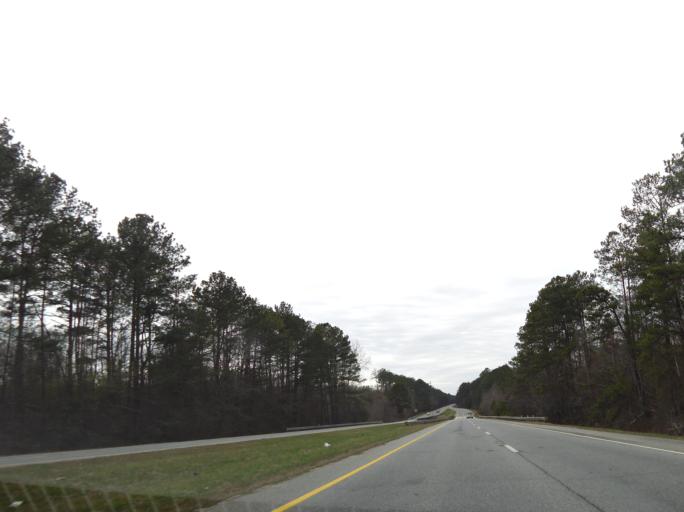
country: US
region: Georgia
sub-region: Bibb County
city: West Point
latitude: 32.7992
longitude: -83.7543
